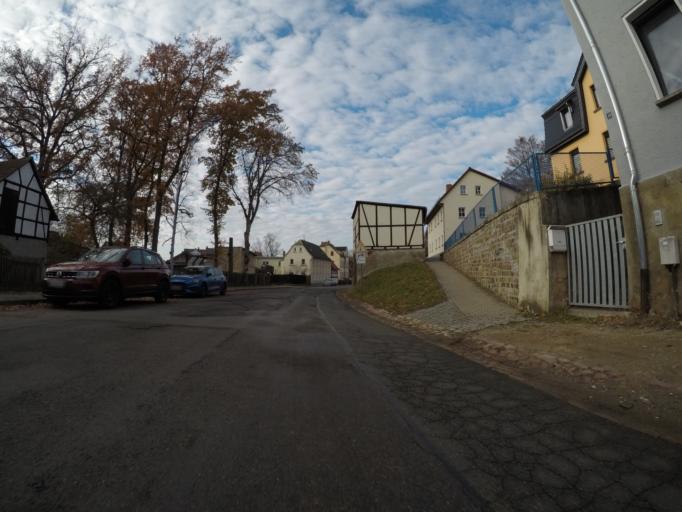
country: DE
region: Thuringia
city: Ponitz
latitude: 50.8554
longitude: 12.4251
